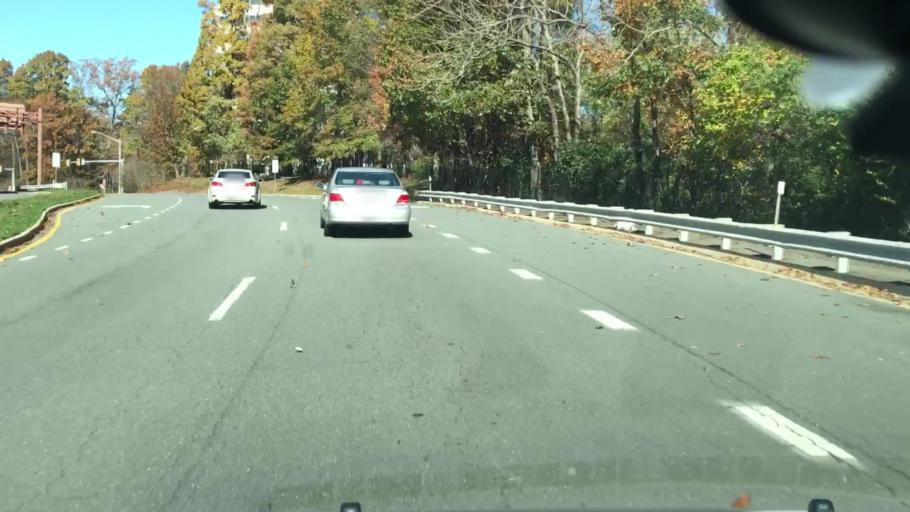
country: US
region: Virginia
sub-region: Fairfax County
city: Merrifield
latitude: 38.8674
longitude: -77.2139
